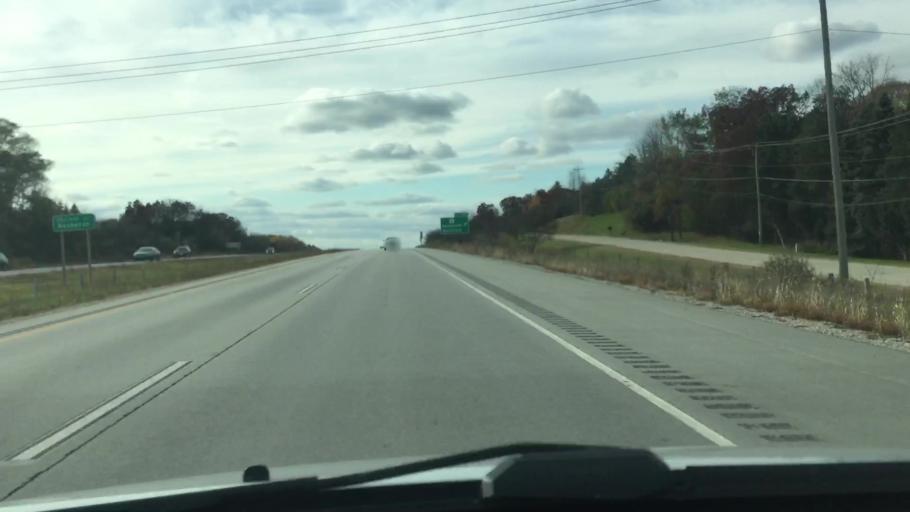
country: US
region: Wisconsin
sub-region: Waukesha County
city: Nashotah
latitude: 43.1023
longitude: -88.3927
